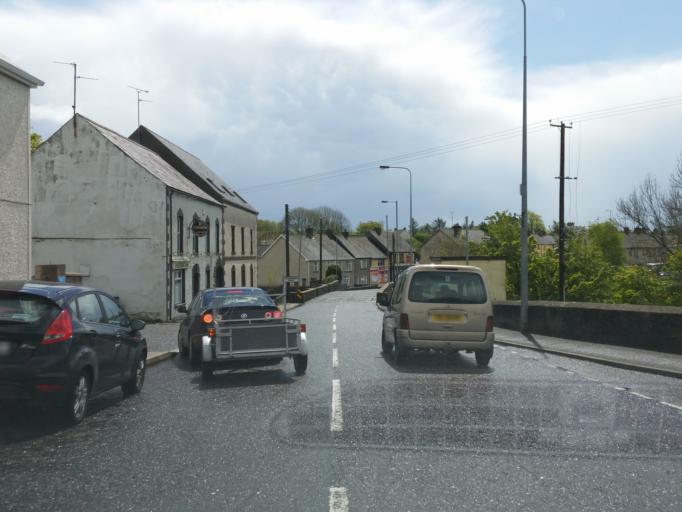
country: GB
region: Northern Ireland
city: Lisnaskea
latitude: 54.2955
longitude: -7.4657
